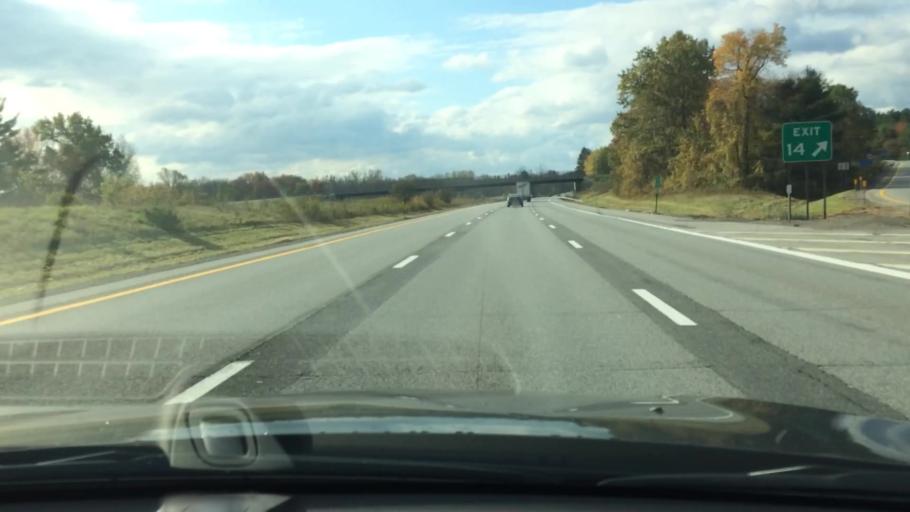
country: US
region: New York
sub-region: Saratoga County
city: Saratoga Springs
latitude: 43.0740
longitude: -73.7505
